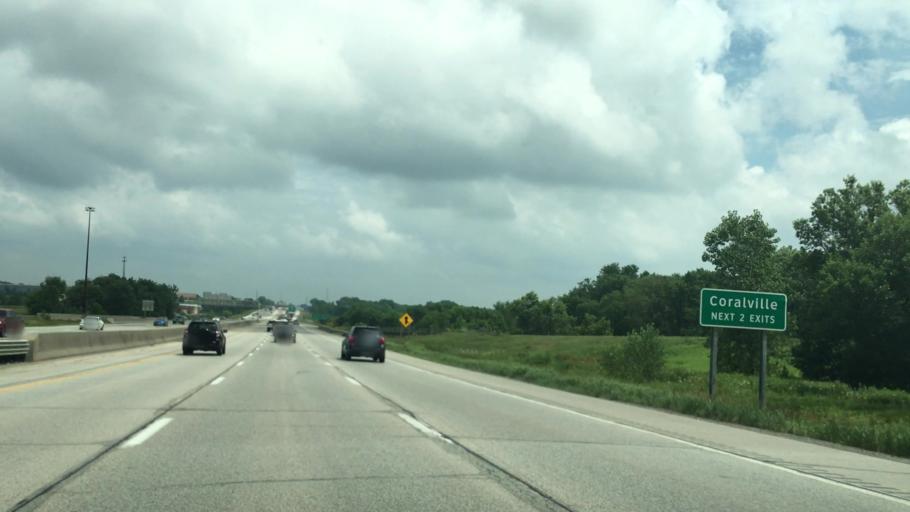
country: US
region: Iowa
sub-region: Johnson County
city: Tiffin
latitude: 41.6943
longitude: -91.6346
